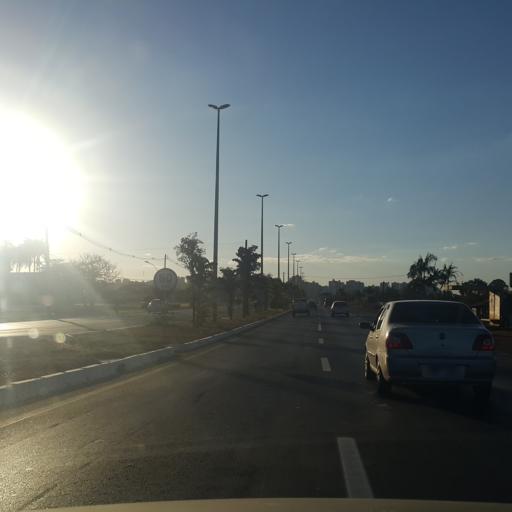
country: BR
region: Federal District
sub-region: Brasilia
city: Brasilia
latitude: -15.8541
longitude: -47.9930
